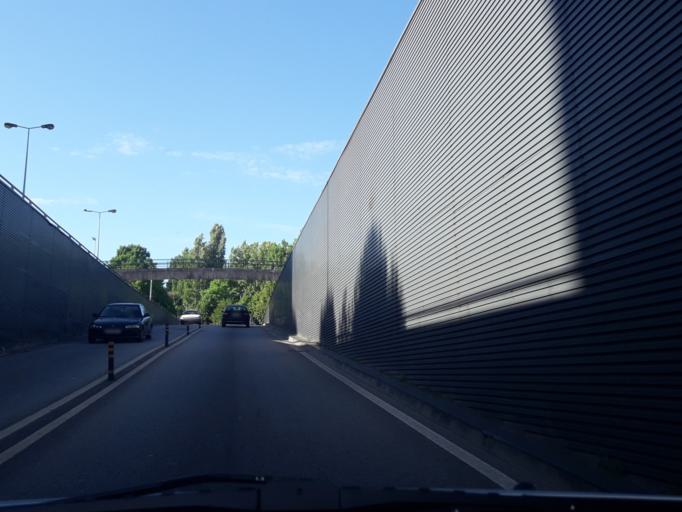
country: PT
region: Braga
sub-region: Vila Nova de Famalicao
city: Vila Nova de Famalicao
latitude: 41.4101
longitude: -8.5168
